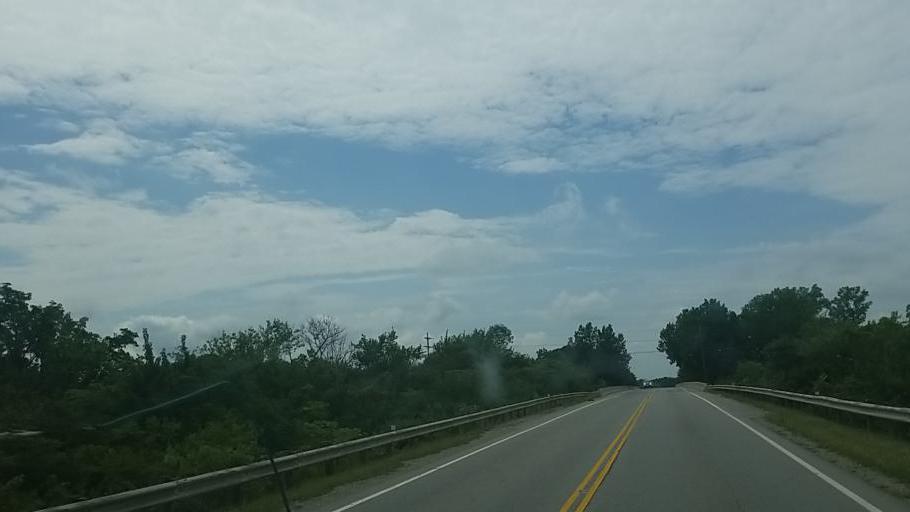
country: US
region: Ohio
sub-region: Franklin County
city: Obetz
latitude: 39.8313
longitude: -82.9530
